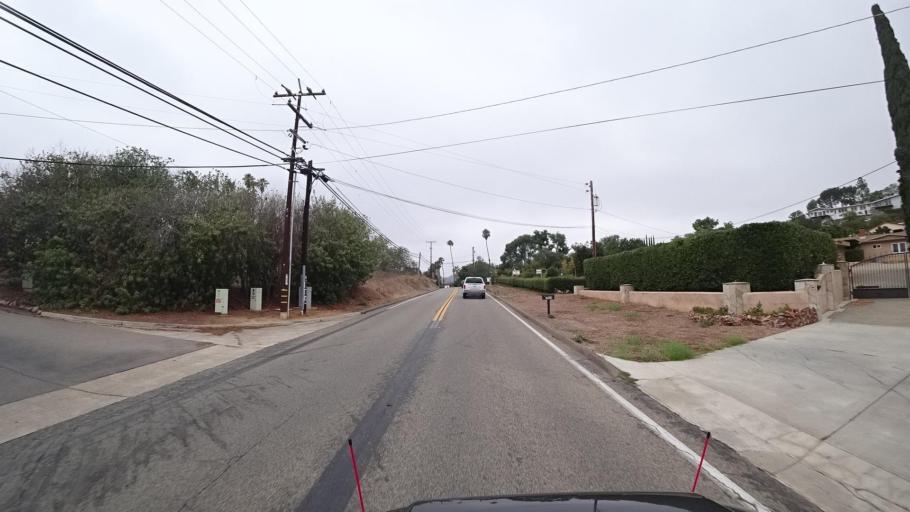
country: US
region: California
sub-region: San Diego County
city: Escondido
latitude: 33.0786
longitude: -117.0993
